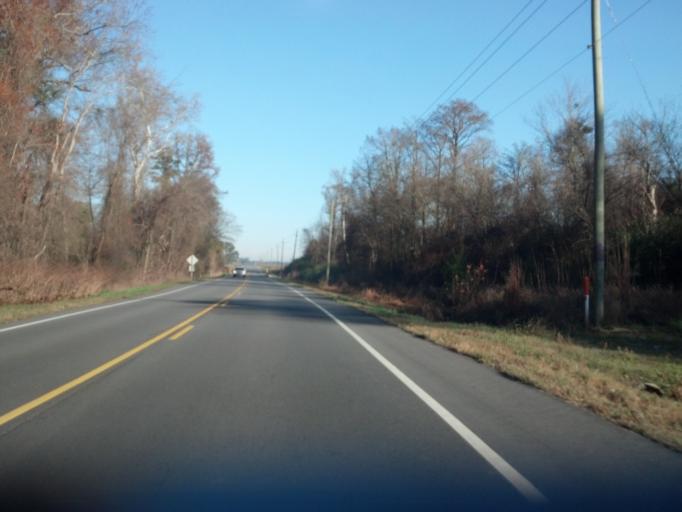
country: US
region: North Carolina
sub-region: Pitt County
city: Ayden
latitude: 35.4589
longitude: -77.4824
